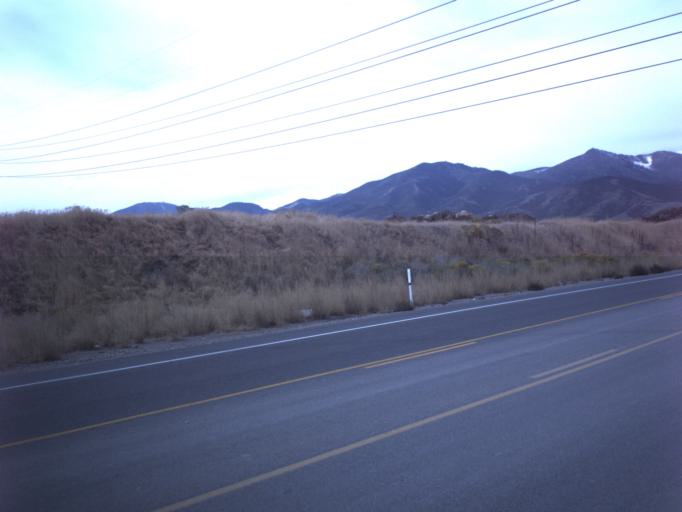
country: US
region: Utah
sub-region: Salt Lake County
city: Oquirrh
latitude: 40.6532
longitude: -112.0583
